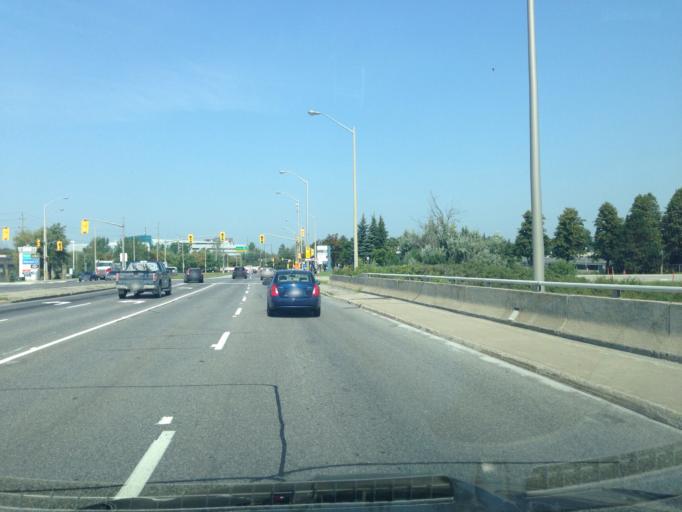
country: CA
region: Ontario
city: Ottawa
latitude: 45.4327
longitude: -75.6066
